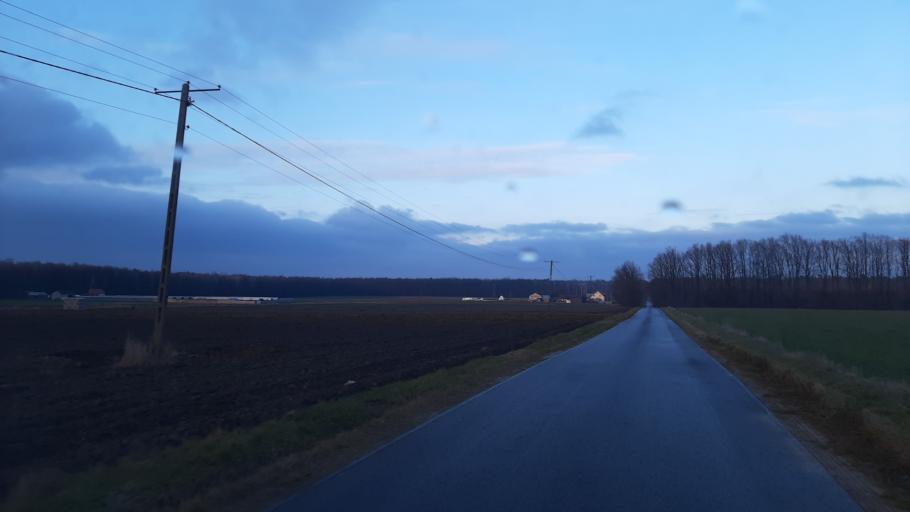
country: PL
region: Lublin Voivodeship
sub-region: Powiat lubelski
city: Garbow
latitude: 51.3662
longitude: 22.3981
